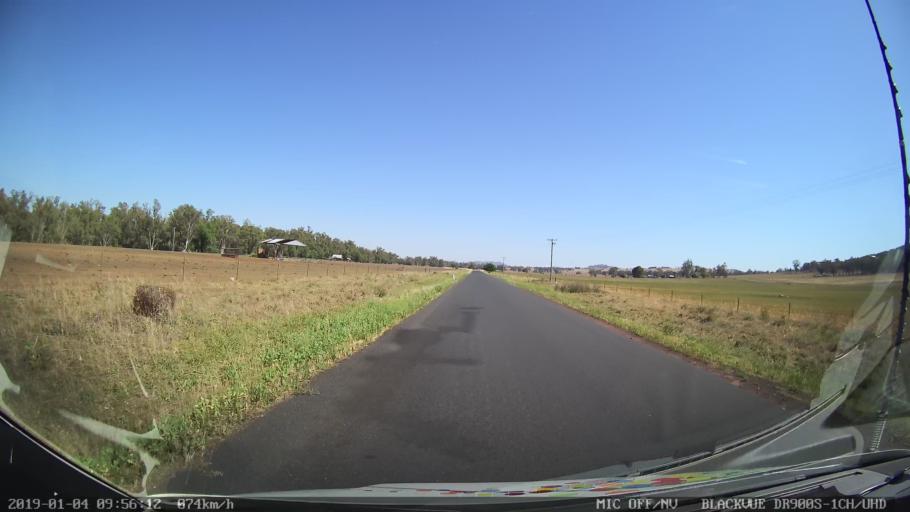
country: AU
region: New South Wales
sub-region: Cabonne
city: Canowindra
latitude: -33.5270
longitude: 148.3995
